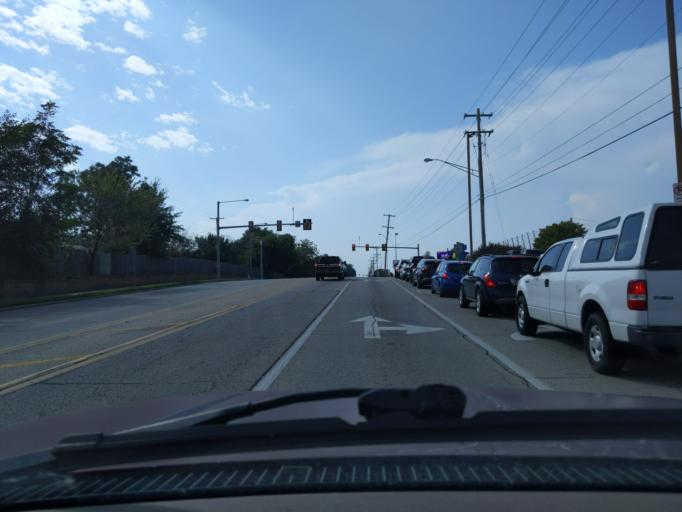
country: US
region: Oklahoma
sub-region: Tulsa County
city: Tulsa
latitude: 36.1333
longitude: -95.9265
